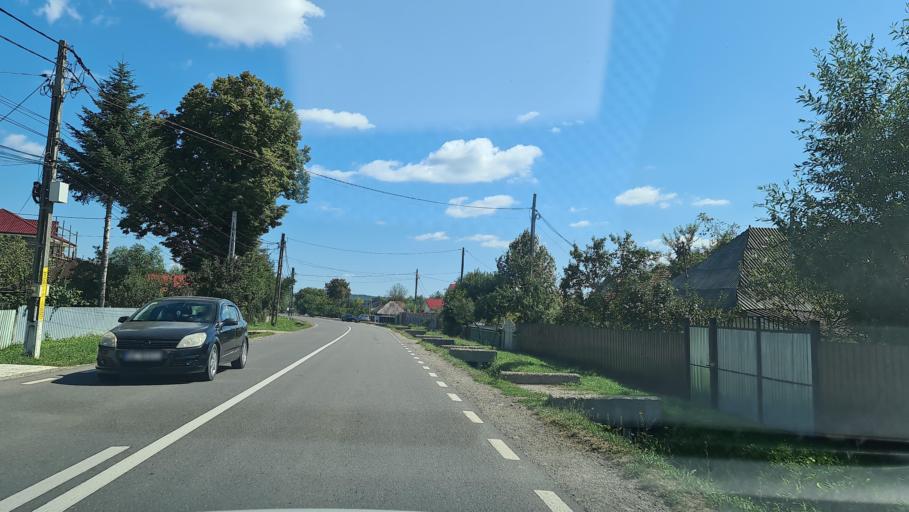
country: RO
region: Bacau
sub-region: Comuna Ardeoani
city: Ardeoani
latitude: 46.5326
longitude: 26.6269
